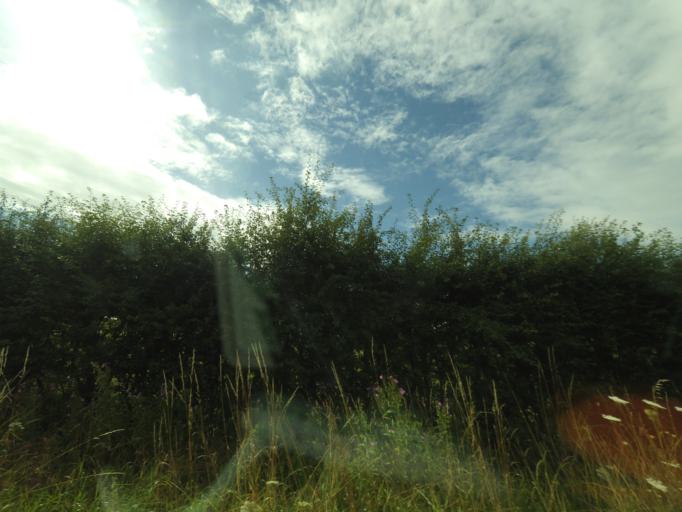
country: DK
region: South Denmark
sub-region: Nordfyns Kommune
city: Sonderso
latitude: 55.4522
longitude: 10.1877
